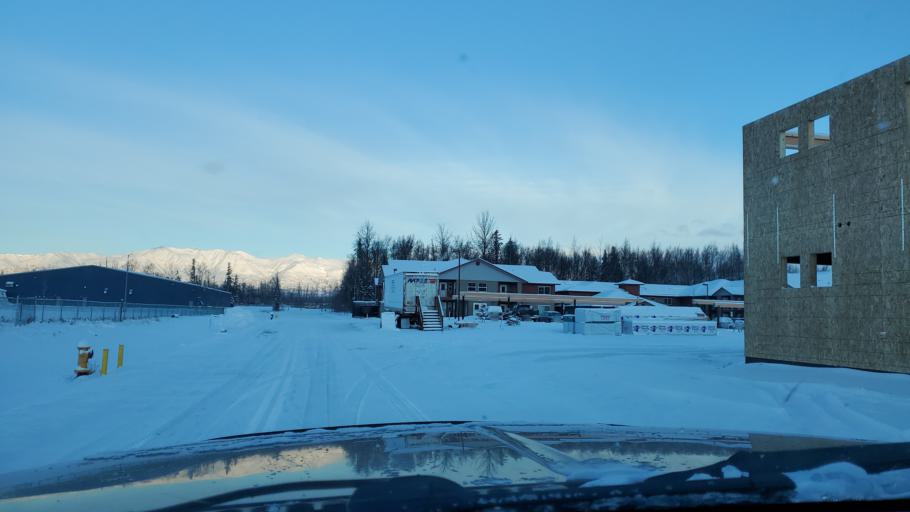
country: US
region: Alaska
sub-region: Matanuska-Susitna Borough
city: Palmer
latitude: 61.5910
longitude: -149.1039
